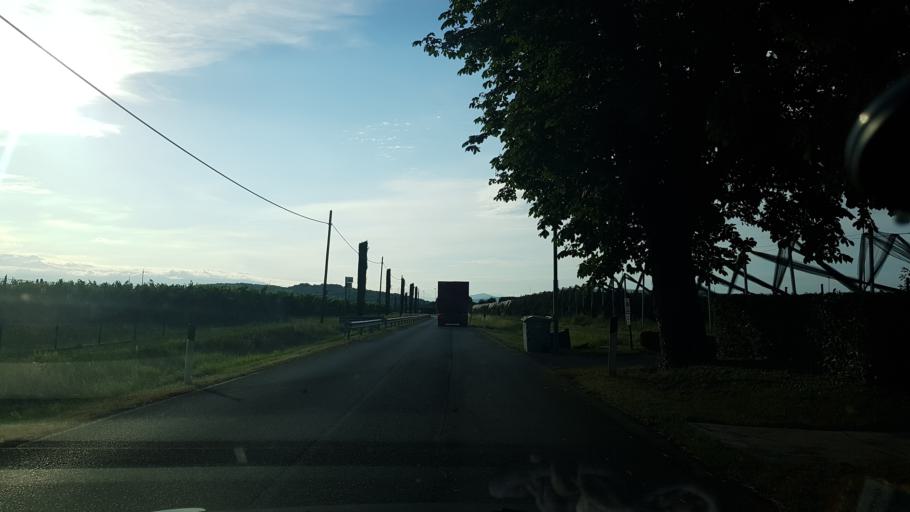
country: IT
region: Friuli Venezia Giulia
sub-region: Provincia di Udine
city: Chiopris
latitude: 45.9231
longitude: 13.3879
